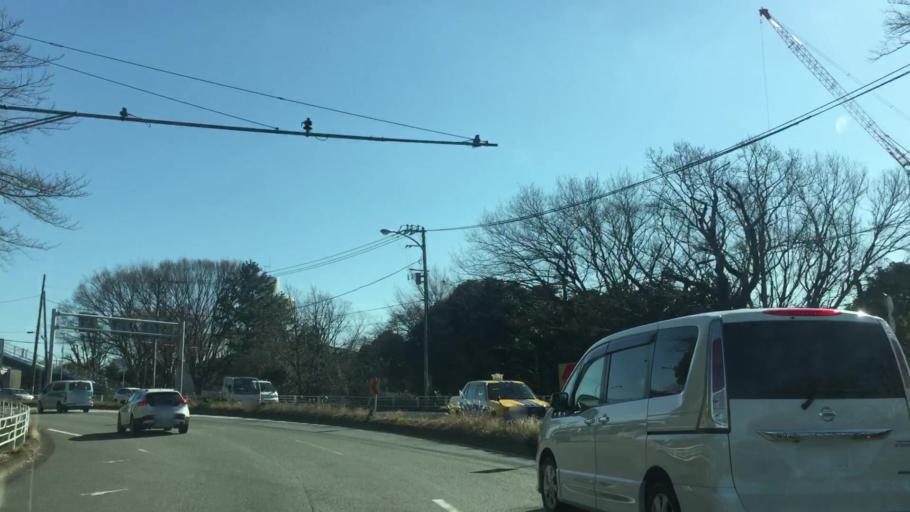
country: JP
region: Kanagawa
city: Yokohama
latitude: 35.4712
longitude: 139.6051
